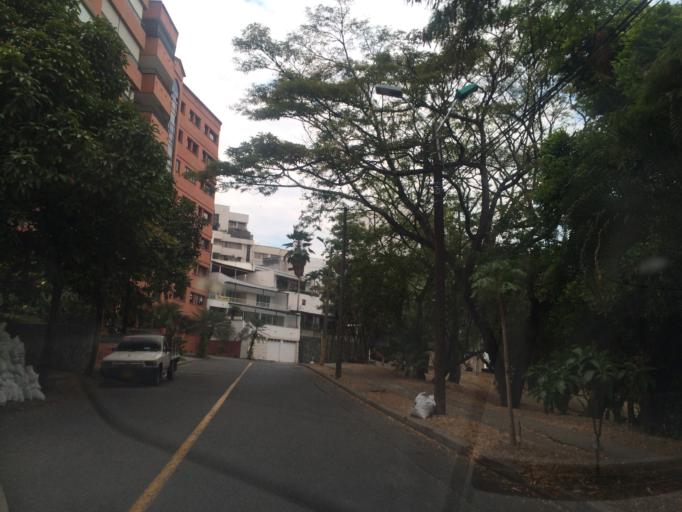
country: CO
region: Valle del Cauca
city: Cali
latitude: 3.4479
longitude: -76.5470
